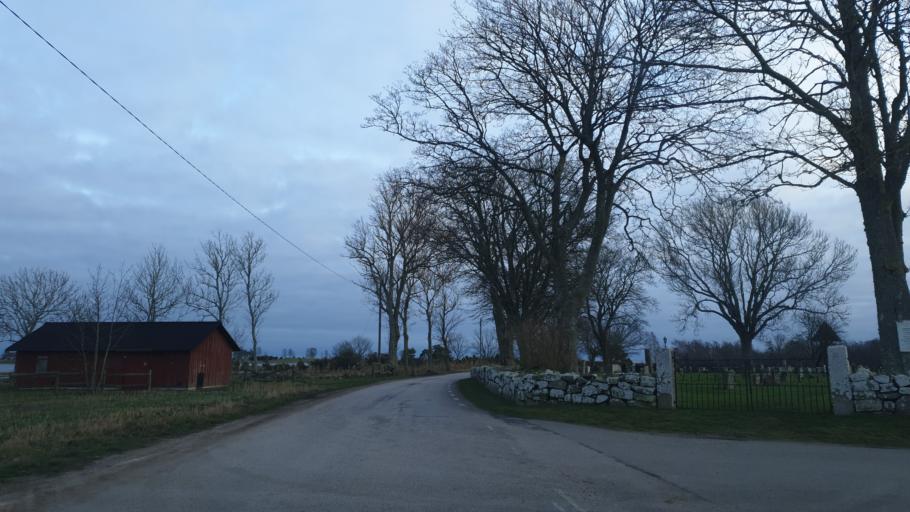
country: SE
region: Kalmar
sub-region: Torsas Kommun
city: Torsas
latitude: 56.2639
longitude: 16.0351
